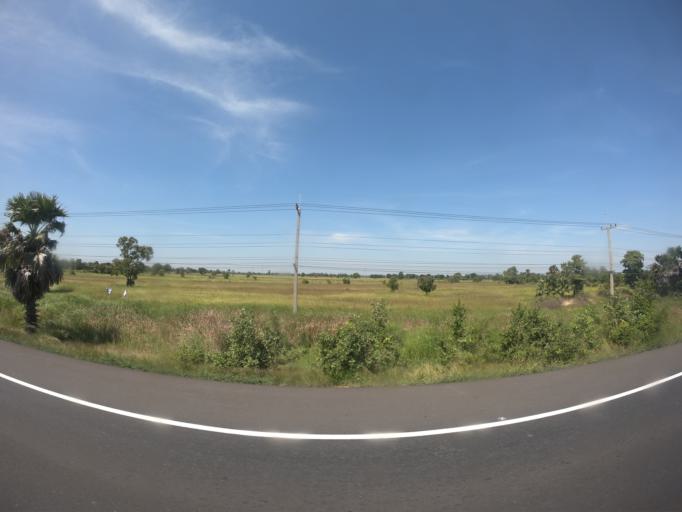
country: TH
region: Nakhon Ratchasima
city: Non Daeng
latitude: 15.4718
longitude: 102.5101
